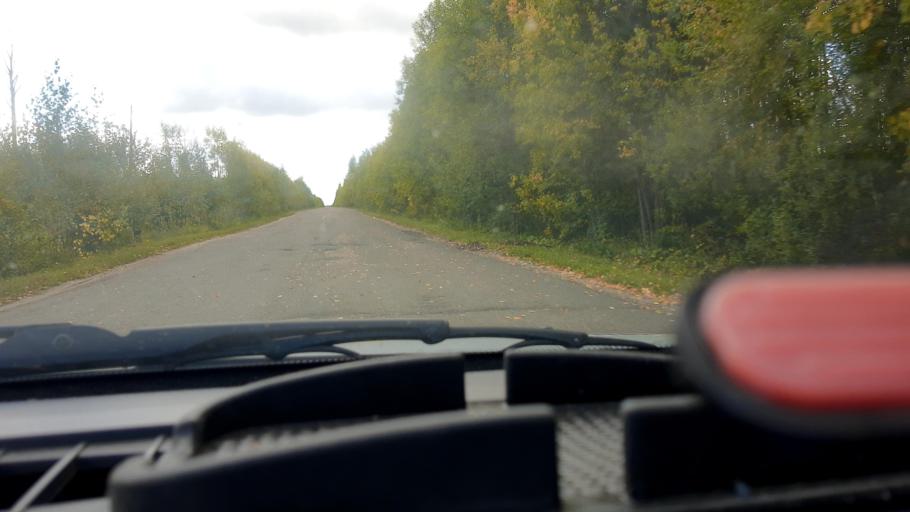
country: RU
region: Mariy-El
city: Kilemary
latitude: 56.9034
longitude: 46.7391
